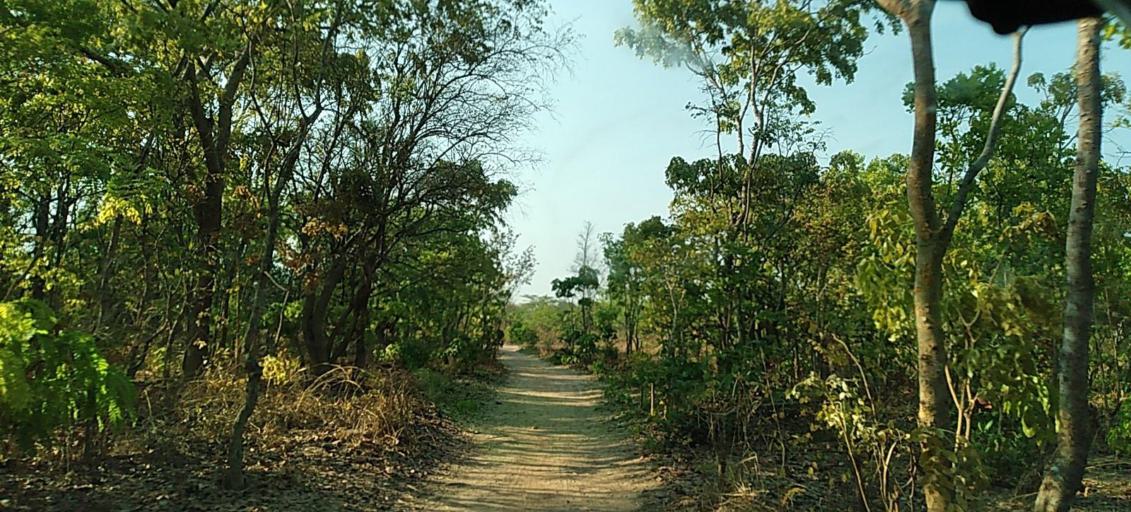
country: ZM
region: North-Western
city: Kalengwa
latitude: -13.1781
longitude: 25.0400
